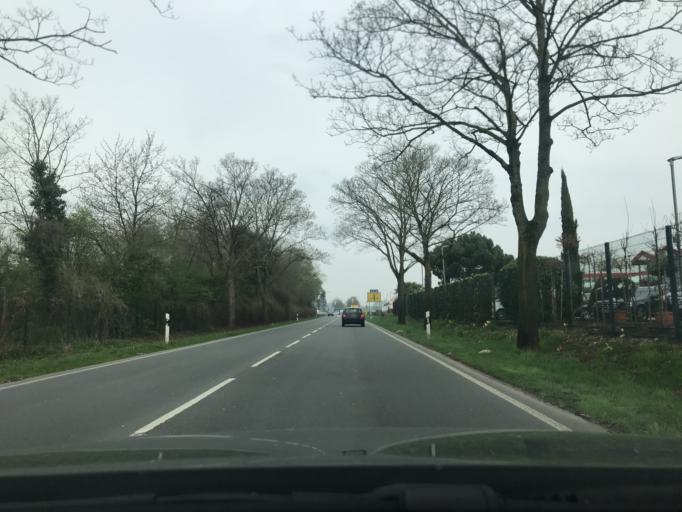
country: DE
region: North Rhine-Westphalia
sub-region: Regierungsbezirk Dusseldorf
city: Kevelaer
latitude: 51.5871
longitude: 6.2492
